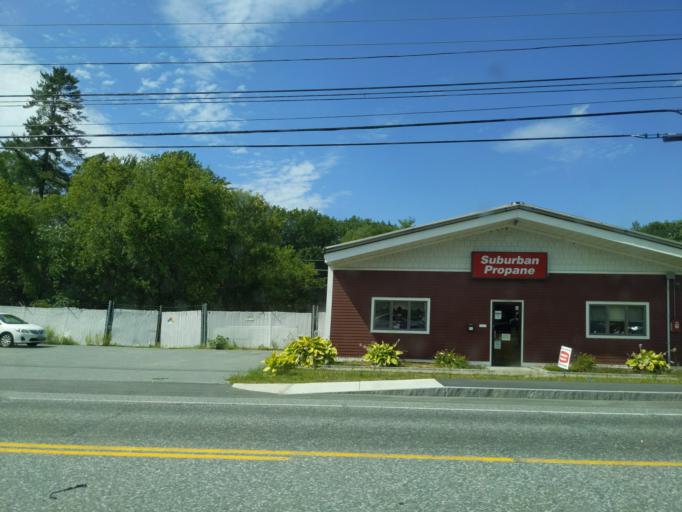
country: US
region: Vermont
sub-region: Windsor County
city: White River Junction
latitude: 43.6359
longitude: -72.2927
